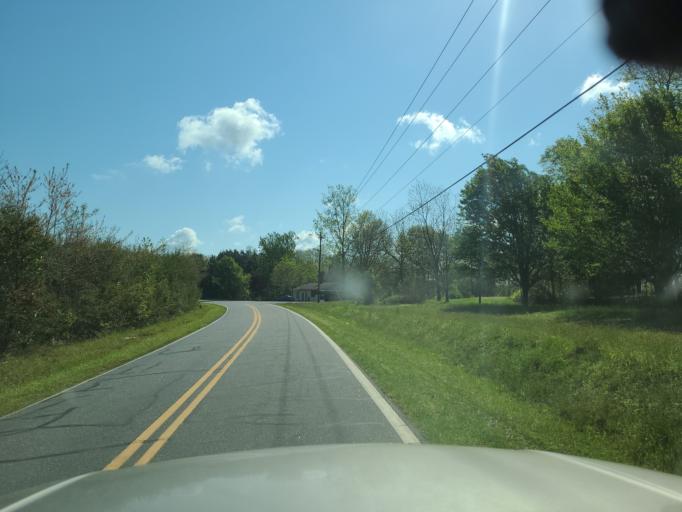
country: US
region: North Carolina
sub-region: Rutherford County
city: Spindale
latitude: 35.2959
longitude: -81.9527
